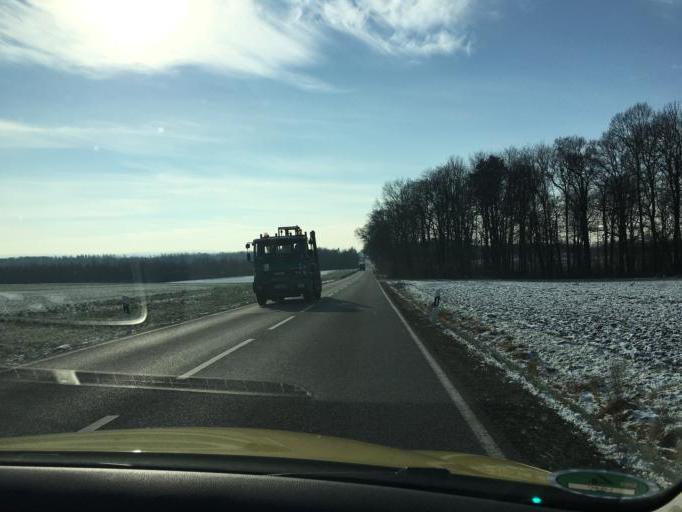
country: DE
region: Saxony
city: Penig
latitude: 50.9663
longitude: 12.6944
